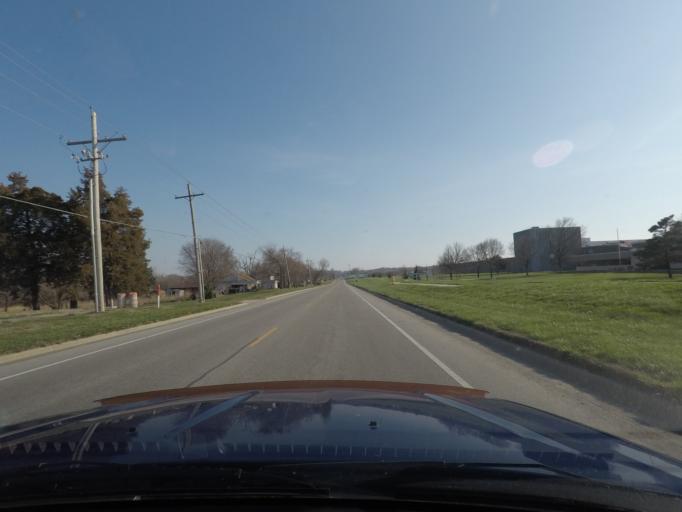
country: US
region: Kansas
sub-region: Douglas County
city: Lawrence
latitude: 38.9972
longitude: -95.2605
